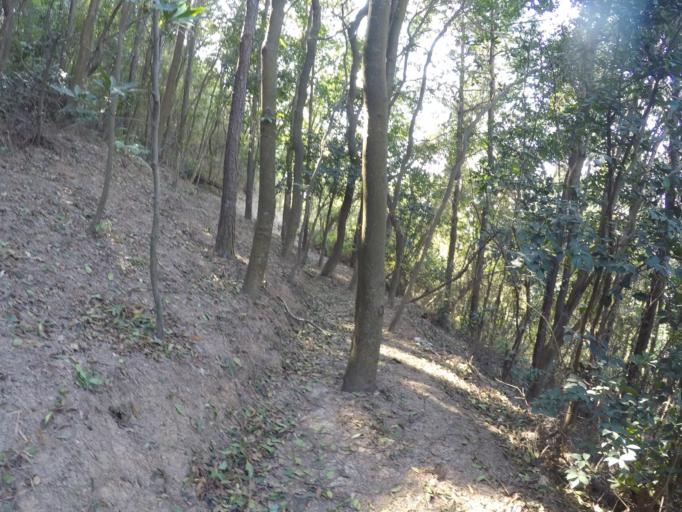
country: CN
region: Guangdong
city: Huancheng
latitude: 22.4664
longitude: 113.4086
